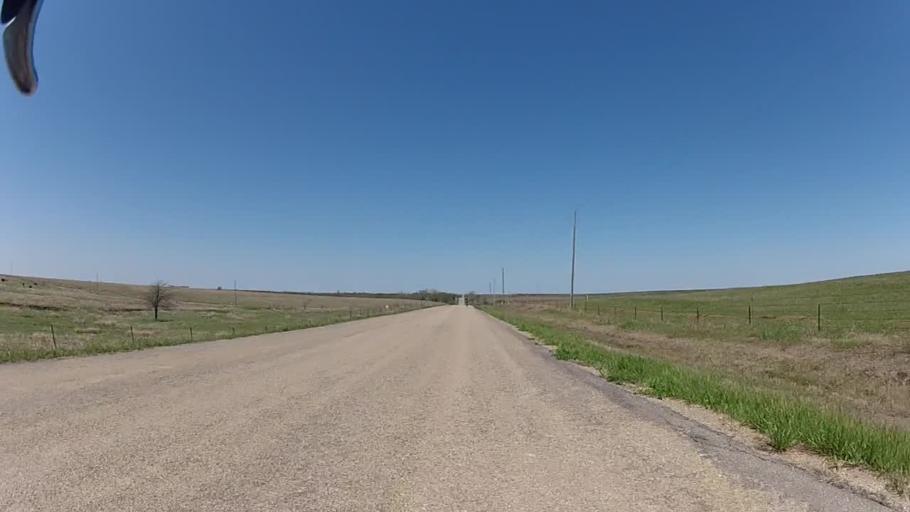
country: US
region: Kansas
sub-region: Riley County
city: Manhattan
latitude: 38.9717
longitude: -96.5370
